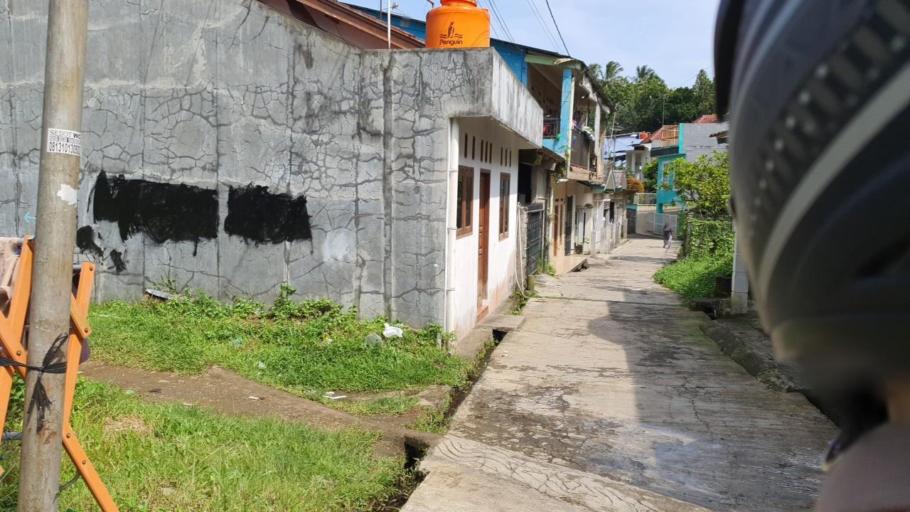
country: ID
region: West Java
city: Caringin
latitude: -6.6530
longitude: 106.9069
